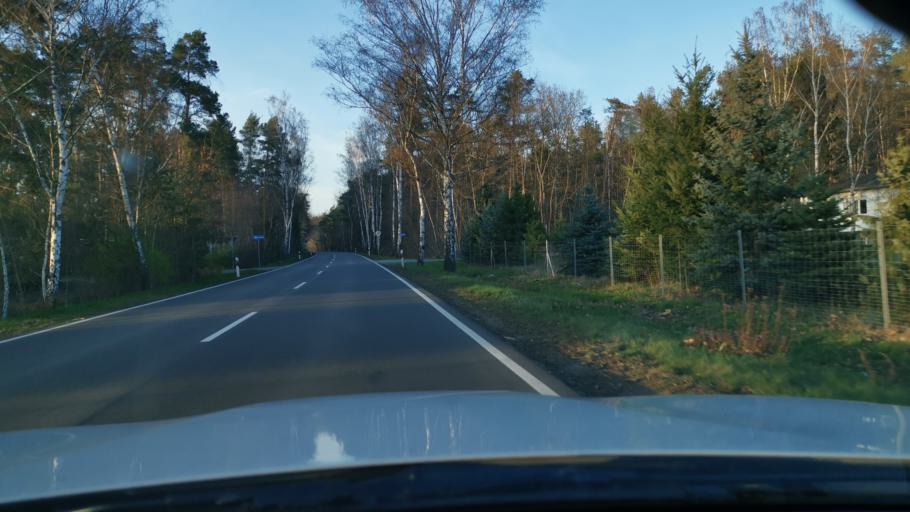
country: DE
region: Saxony
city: Bad Duben
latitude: 51.6168
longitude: 12.5887
